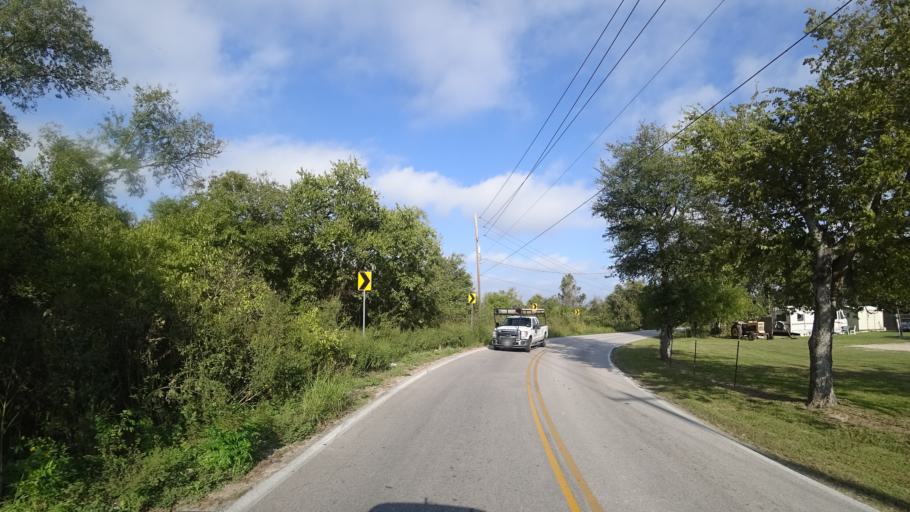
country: US
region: Texas
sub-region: Travis County
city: Pflugerville
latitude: 30.3538
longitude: -97.6476
